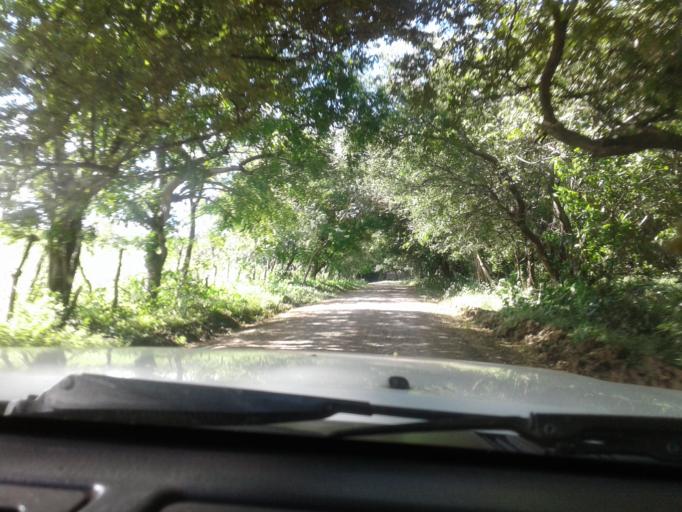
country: NI
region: Rivas
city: Tola
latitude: 11.4143
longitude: -85.9188
